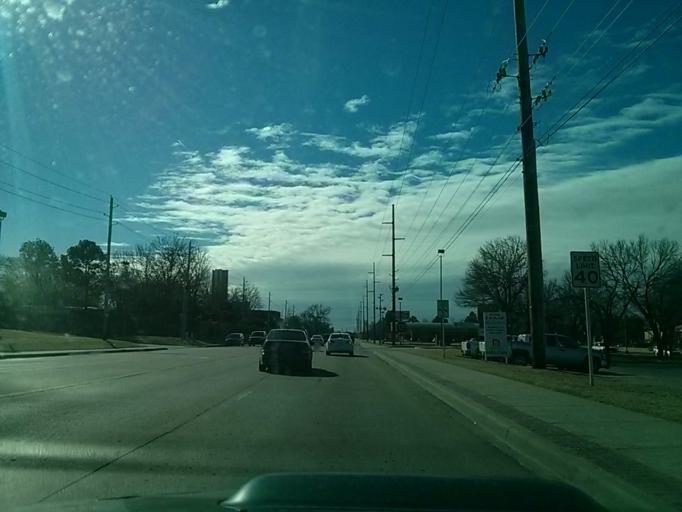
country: US
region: Oklahoma
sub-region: Tulsa County
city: Jenks
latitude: 36.0599
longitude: -95.9579
